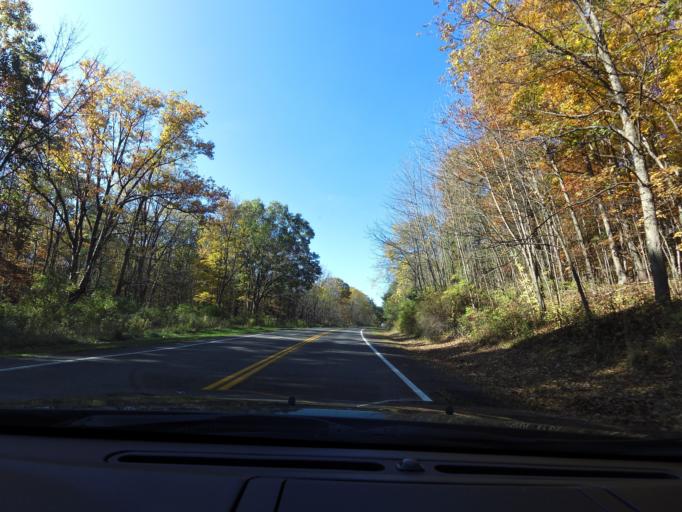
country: US
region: New York
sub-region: Wyoming County
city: Perry
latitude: 42.6840
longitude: -77.9659
